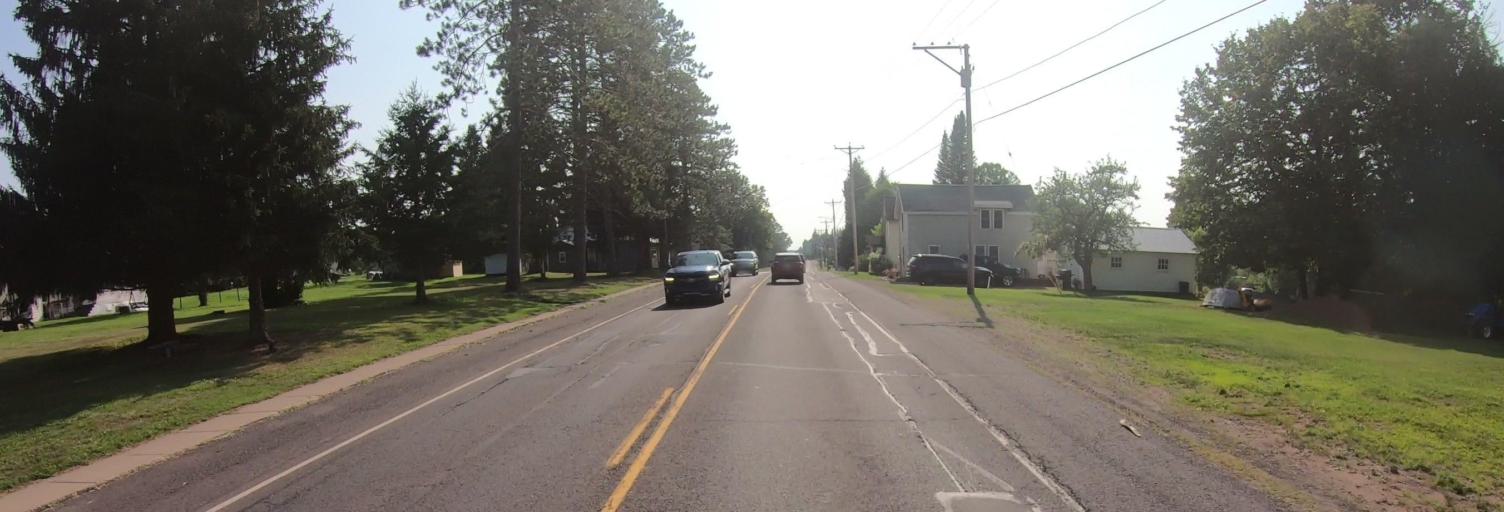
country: US
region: Wisconsin
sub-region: Iron County
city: Hurley
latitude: 46.4408
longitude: -90.2061
